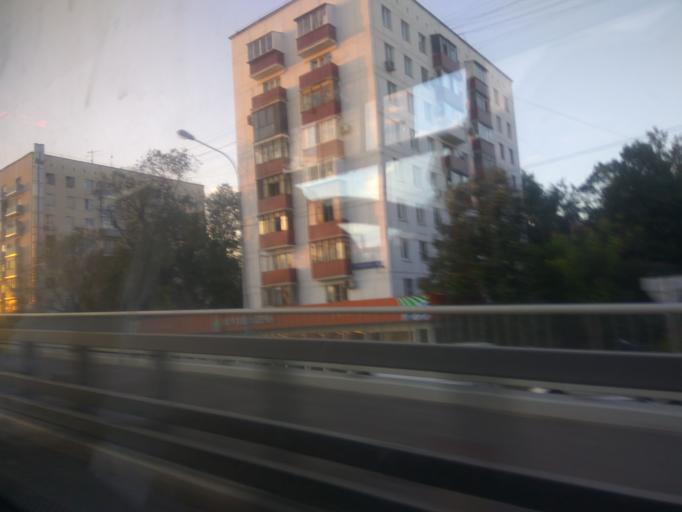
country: RU
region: Moskovskaya
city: Koptevo
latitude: 55.8099
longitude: 37.4919
